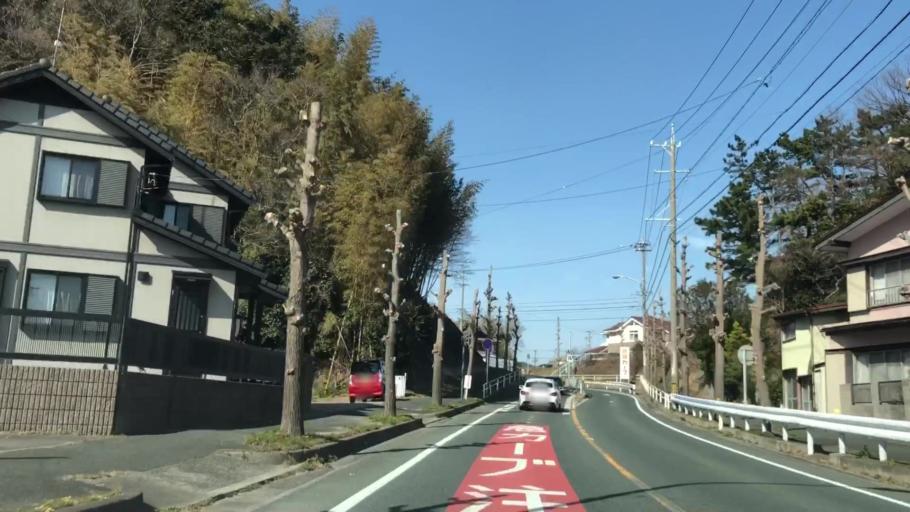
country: JP
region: Aichi
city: Gamagori
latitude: 34.8168
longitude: 137.2370
